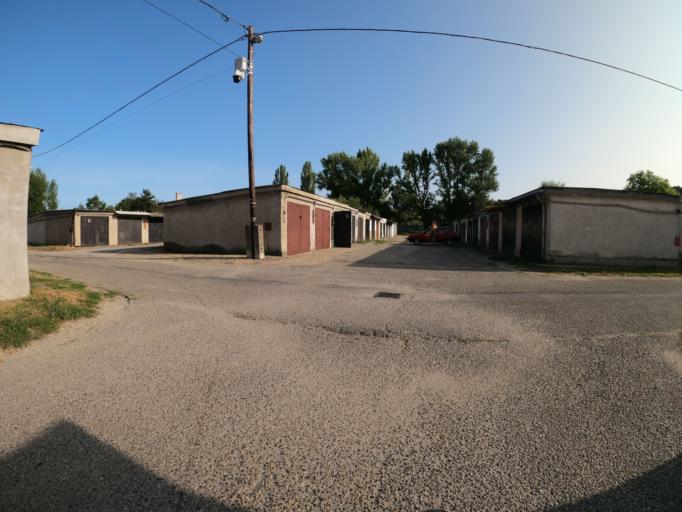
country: HU
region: Borsod-Abauj-Zemplen
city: Miskolc
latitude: 48.0941
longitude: 20.7073
